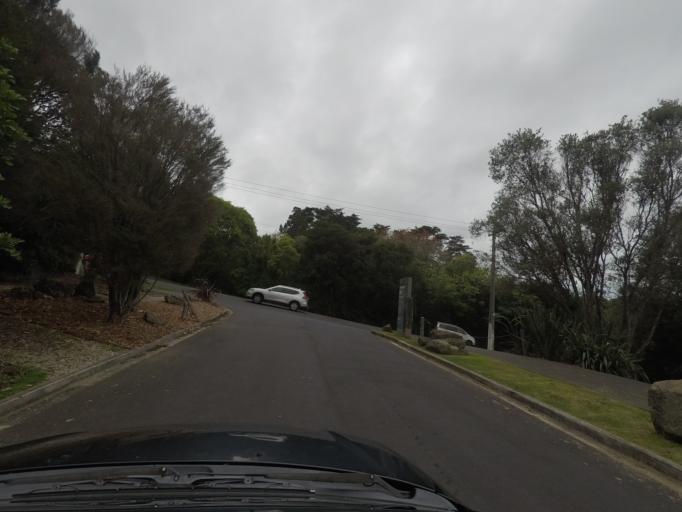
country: NZ
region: Auckland
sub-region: Auckland
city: Auckland
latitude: -36.8639
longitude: 174.7853
